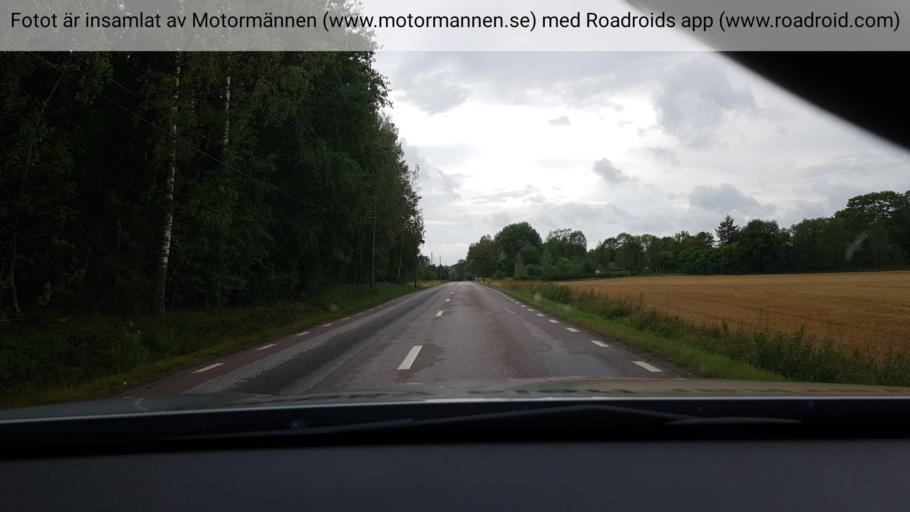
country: SE
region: Uppsala
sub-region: Heby Kommun
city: OEstervala
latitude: 60.1701
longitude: 17.1056
